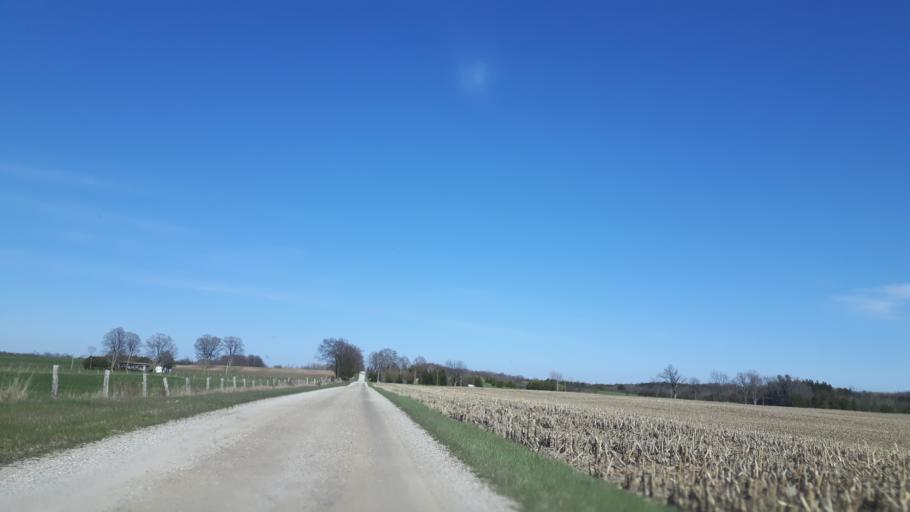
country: CA
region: Ontario
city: Goderich
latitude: 43.6613
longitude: -81.6900
